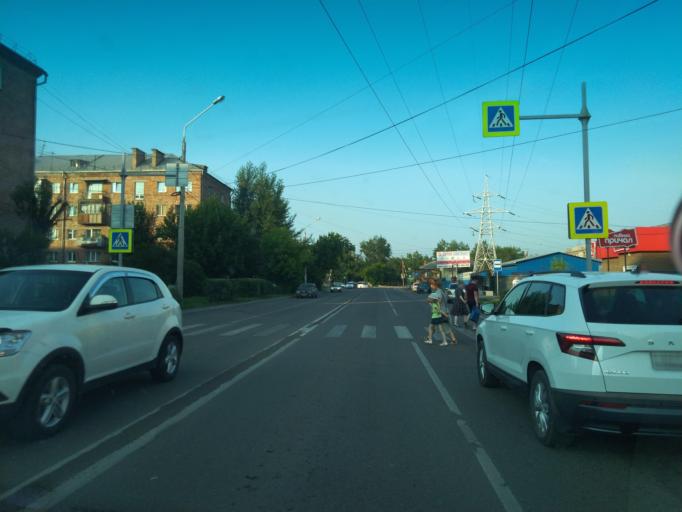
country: RU
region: Krasnoyarskiy
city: Krasnoyarsk
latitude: 56.0037
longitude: 92.9537
